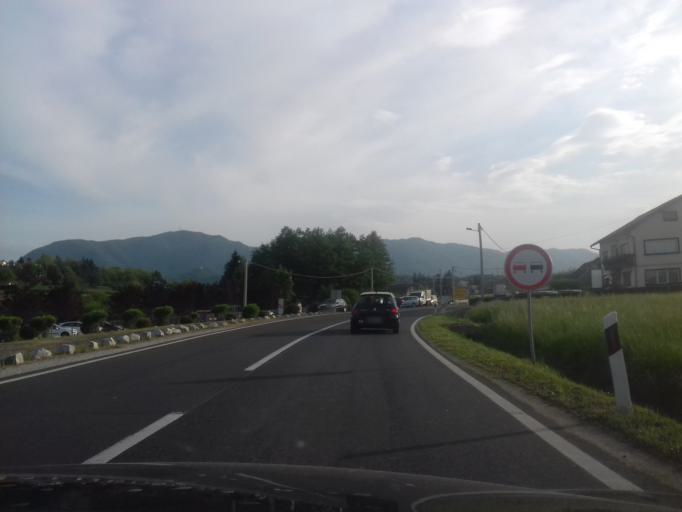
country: HR
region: Varazdinska
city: Ivanec
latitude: 46.2370
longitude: 16.1567
